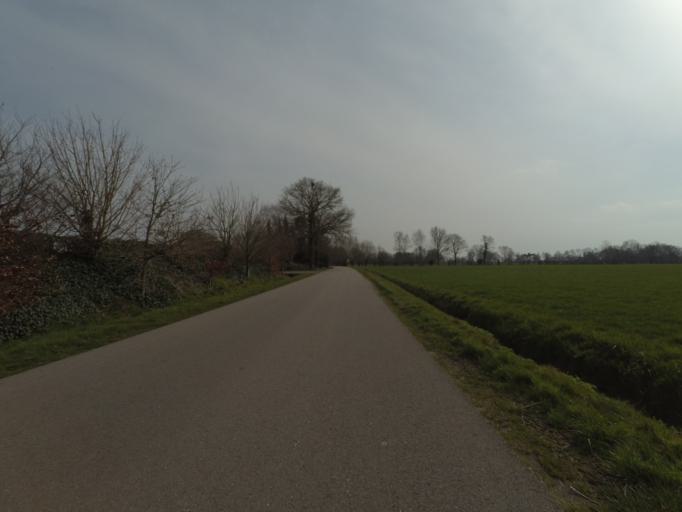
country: NL
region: Gelderland
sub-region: Gemeente Barneveld
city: Barneveld
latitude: 52.1053
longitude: 5.5697
